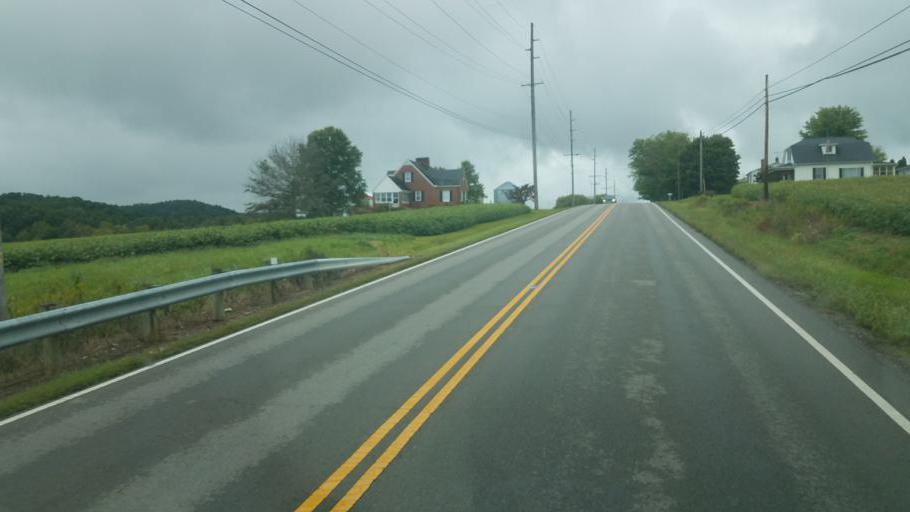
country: US
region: Ohio
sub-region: Scioto County
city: Wheelersburg
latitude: 38.7695
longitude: -82.7874
